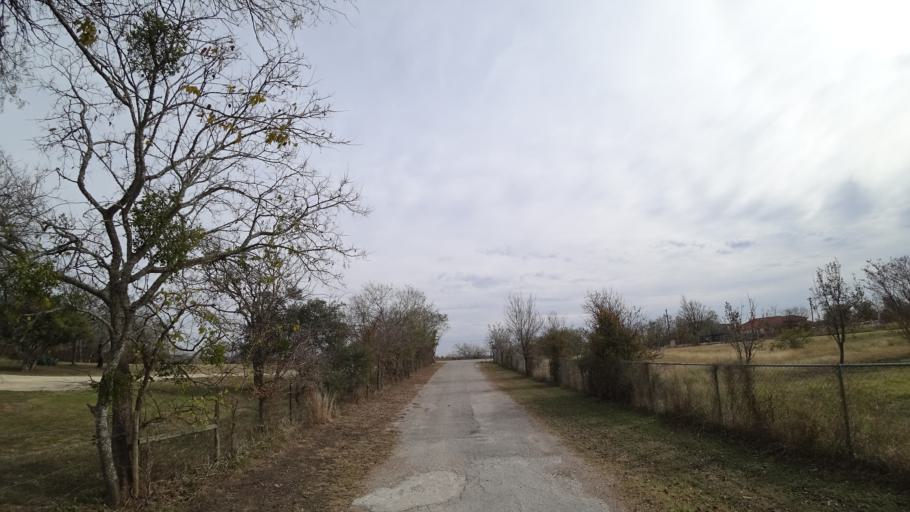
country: US
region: Texas
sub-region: Travis County
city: Garfield
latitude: 30.1458
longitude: -97.5801
